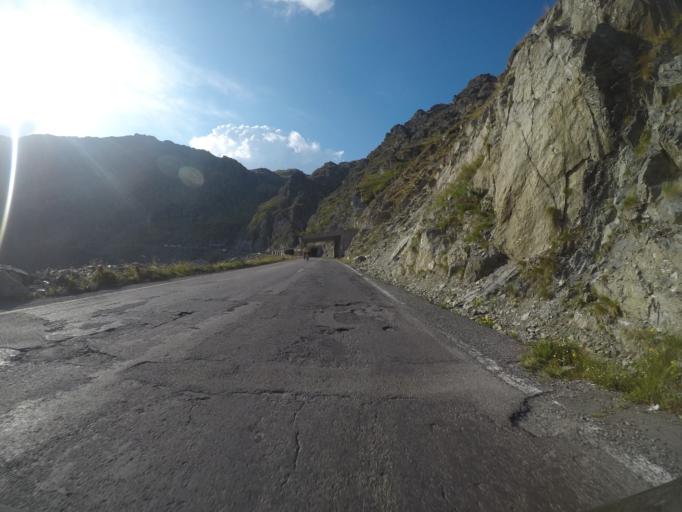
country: RO
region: Sibiu
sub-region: Comuna Cartisoara
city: Cartisoara
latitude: 45.5931
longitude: 24.6241
